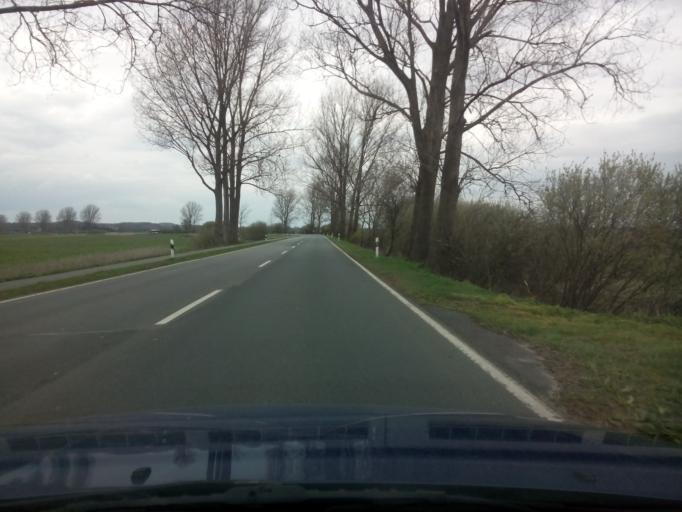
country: DE
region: Lower Saxony
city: Osterholz-Scharmbeck
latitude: 53.2072
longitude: 8.8201
